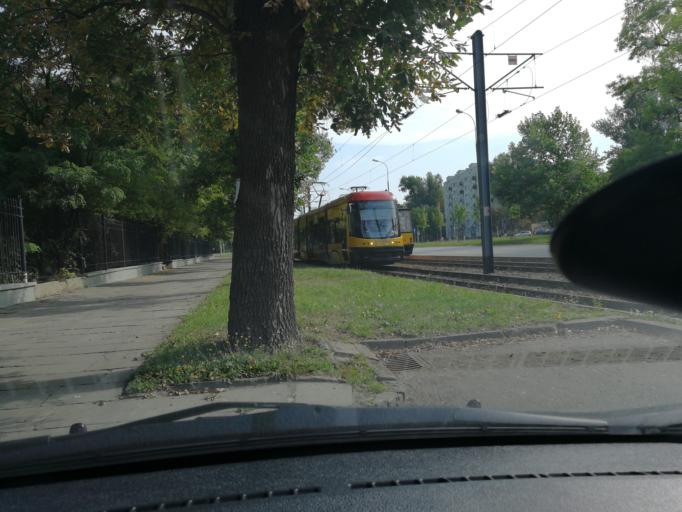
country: PL
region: Masovian Voivodeship
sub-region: Warszawa
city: Ochota
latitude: 52.2287
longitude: 20.9487
